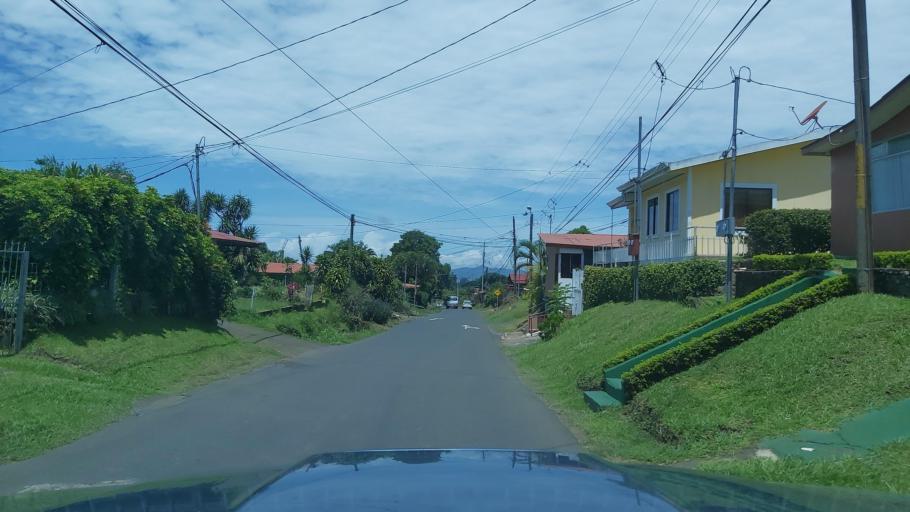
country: CR
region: Alajuela
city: San Juan
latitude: 10.0908
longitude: -84.3412
